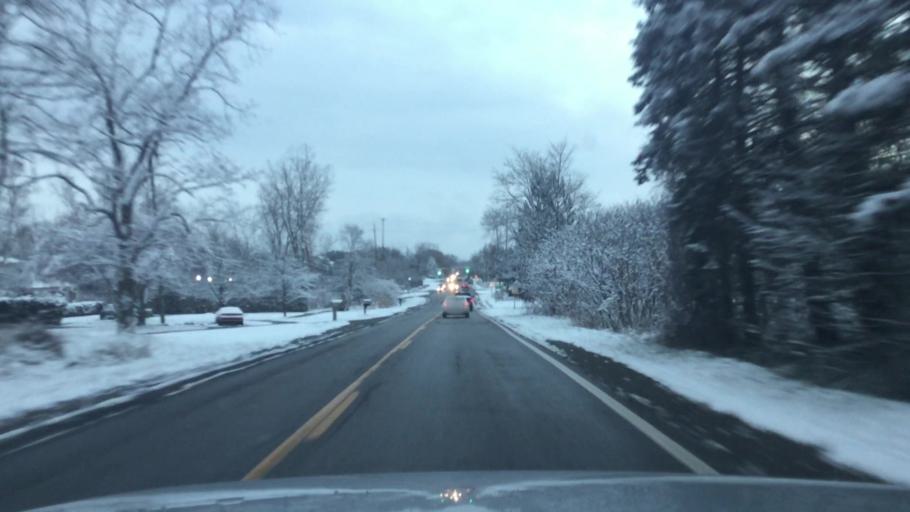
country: US
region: Michigan
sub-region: Oakland County
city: West Bloomfield Township
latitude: 42.6098
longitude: -83.3984
